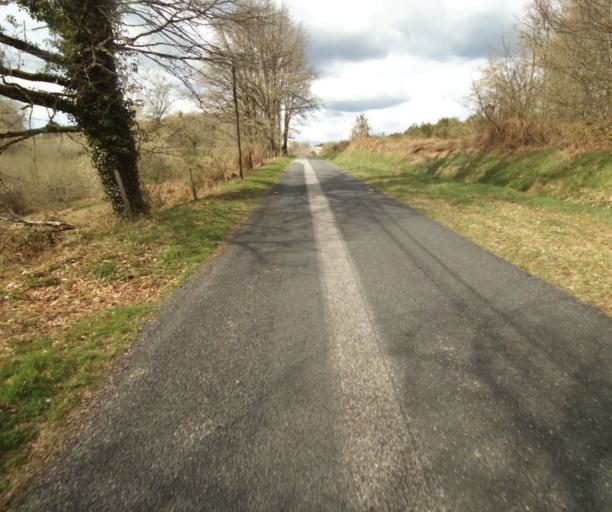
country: FR
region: Limousin
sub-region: Departement de la Correze
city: Argentat
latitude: 45.2085
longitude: 1.9662
